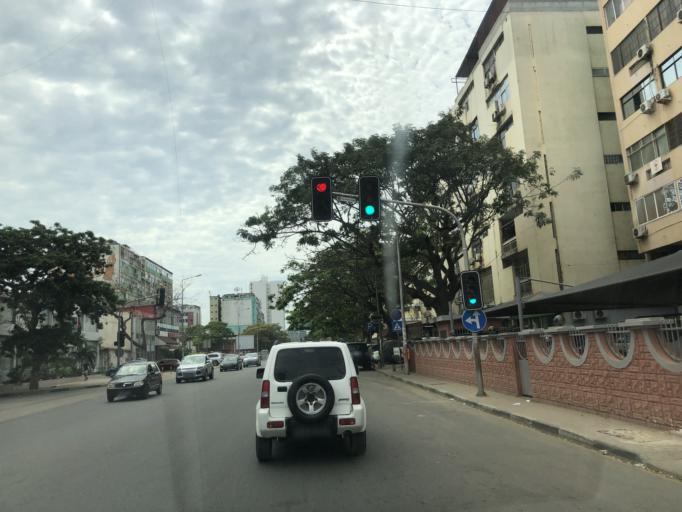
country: AO
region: Luanda
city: Luanda
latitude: -8.8233
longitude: 13.2529
